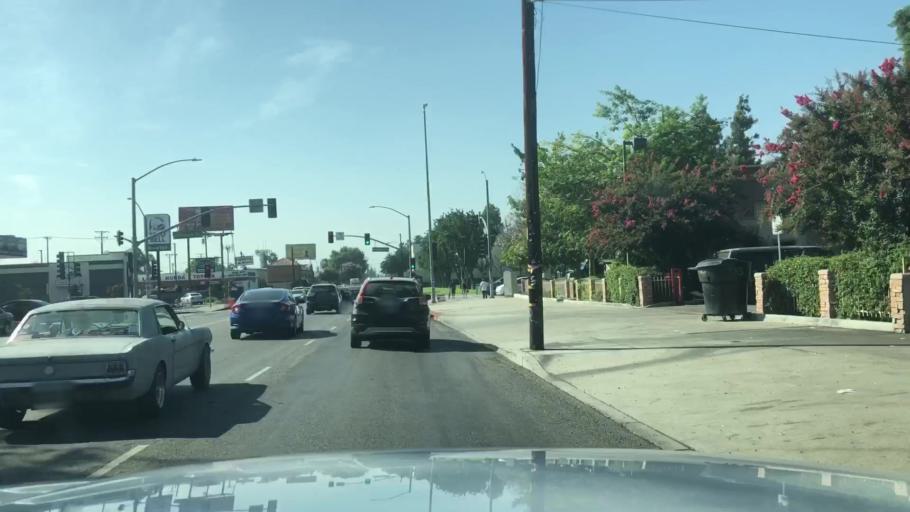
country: US
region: California
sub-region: Los Angeles County
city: West Whittier-Los Nietos
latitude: 33.9895
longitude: -118.0634
